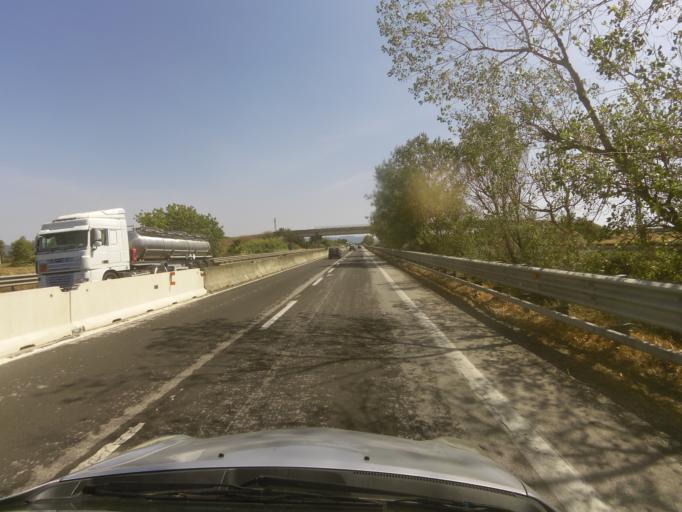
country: IT
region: Tuscany
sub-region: Provincia di Livorno
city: La California
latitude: 43.2600
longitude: 10.5443
